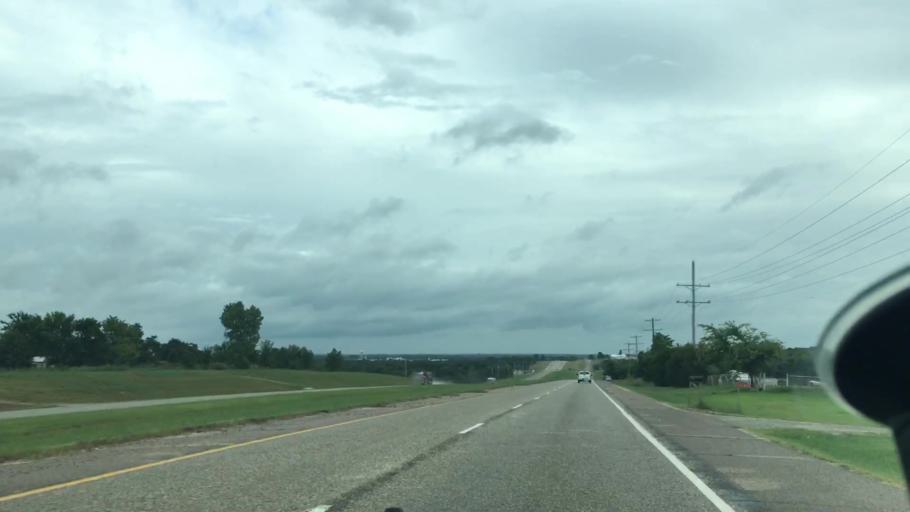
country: US
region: Oklahoma
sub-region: Seminole County
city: Seminole
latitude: 35.2881
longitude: -96.6712
